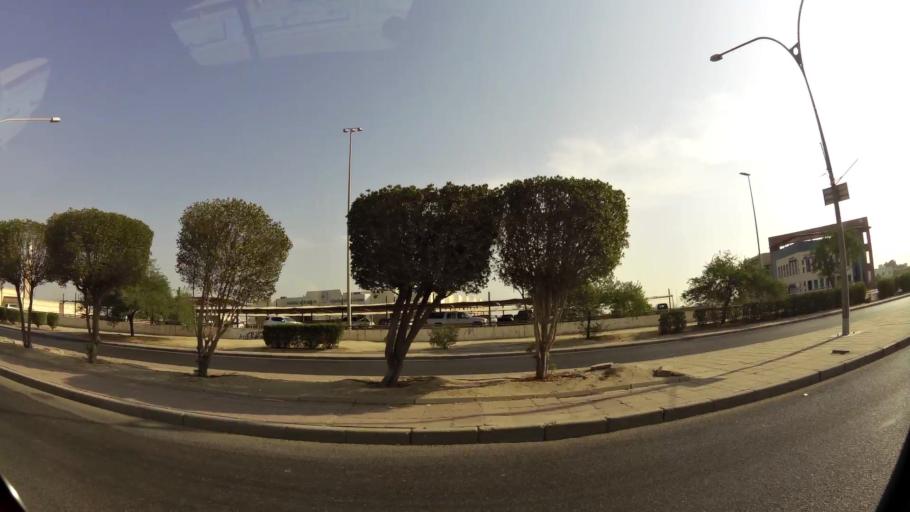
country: KW
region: Mubarak al Kabir
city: Mubarak al Kabir
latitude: 29.1663
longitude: 48.0636
